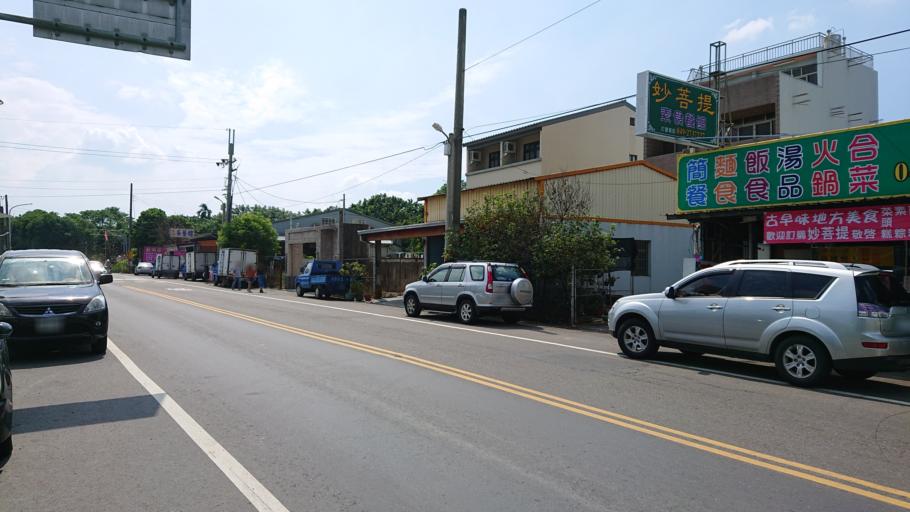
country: TW
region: Taiwan
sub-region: Nantou
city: Nantou
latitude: 23.8351
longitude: 120.7025
